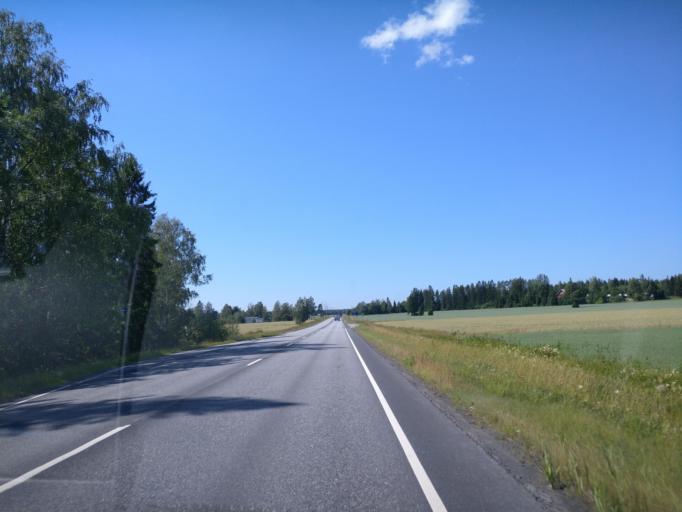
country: FI
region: Satakunta
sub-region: Pori
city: Nakkila
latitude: 61.4589
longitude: 22.0216
